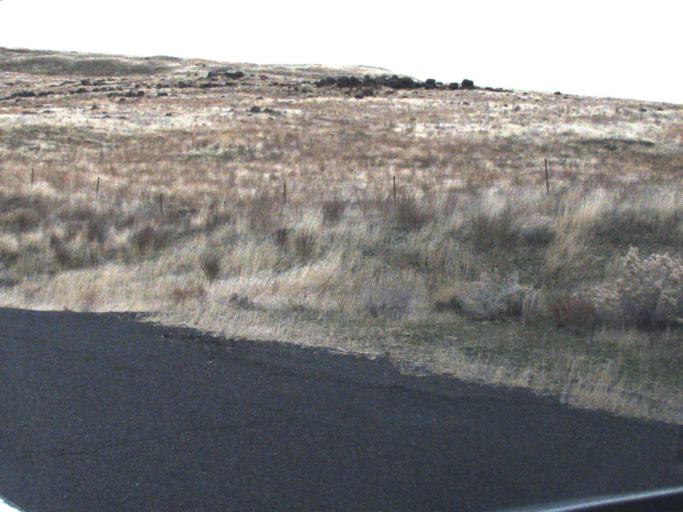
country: US
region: Washington
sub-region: Adams County
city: Ritzville
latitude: 46.7802
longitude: -118.0889
